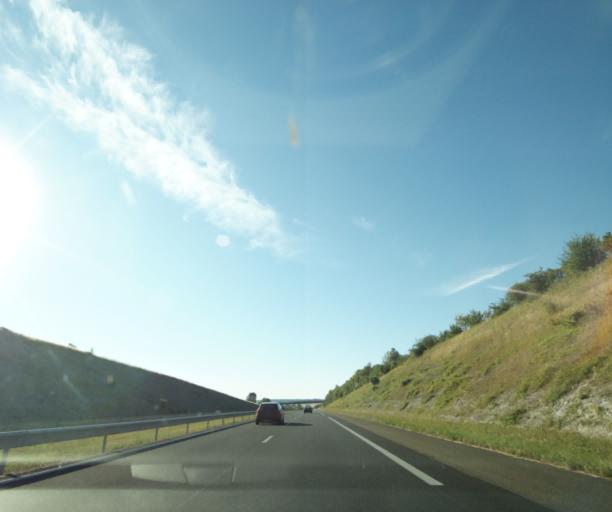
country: FR
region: Bourgogne
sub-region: Departement de l'Yonne
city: Courlon-sur-Yonne
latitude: 48.3327
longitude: 3.2128
